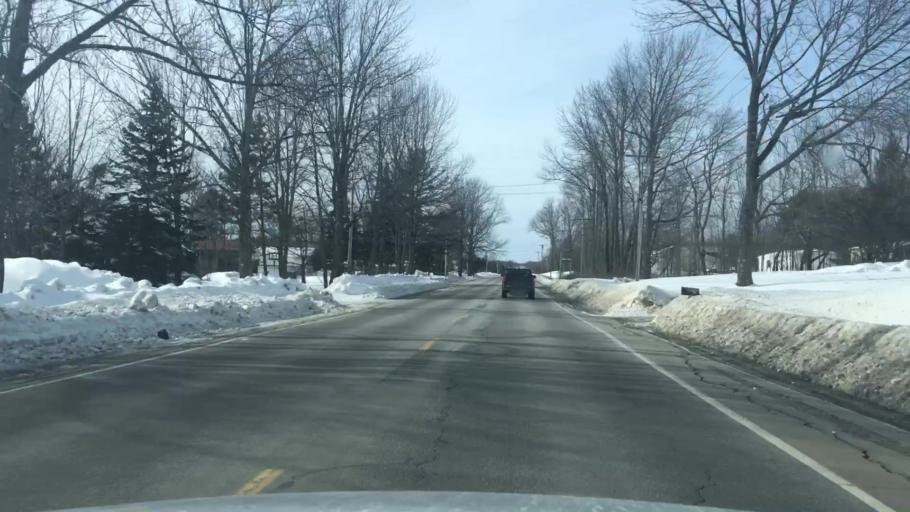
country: US
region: Maine
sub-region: Penobscot County
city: Kenduskeag
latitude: 44.9733
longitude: -68.9817
